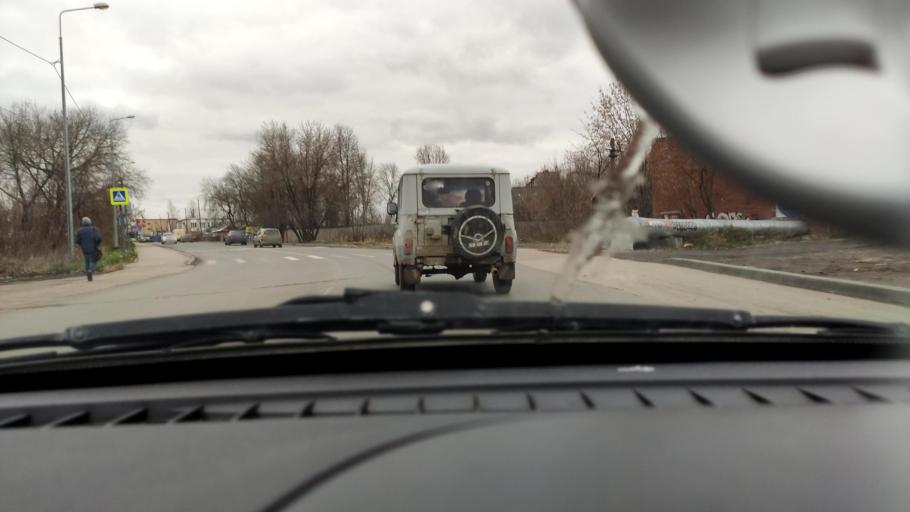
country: RU
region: Perm
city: Kondratovo
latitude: 57.9643
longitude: 56.1541
